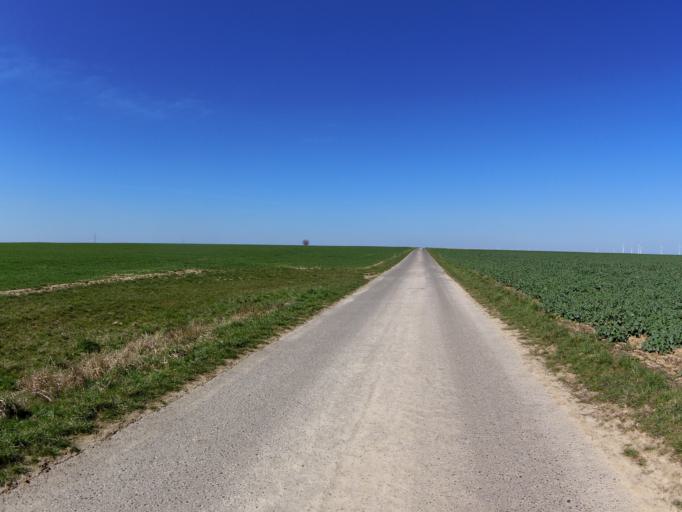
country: DE
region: Bavaria
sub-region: Regierungsbezirk Unterfranken
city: Prosselsheim
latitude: 49.8467
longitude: 10.1242
